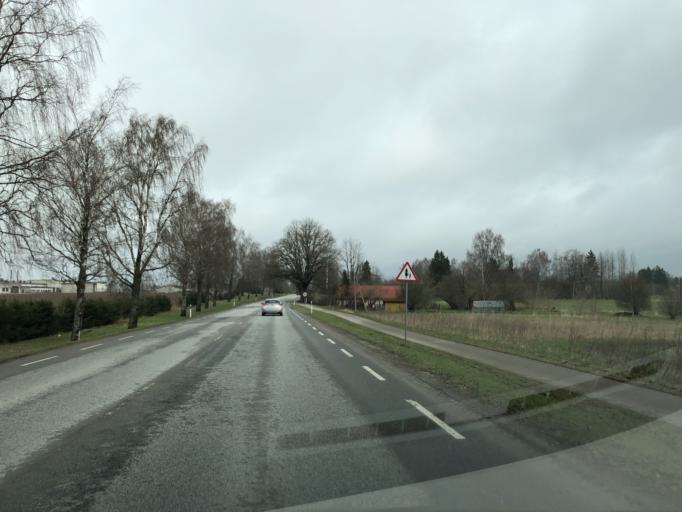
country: EE
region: Jogevamaa
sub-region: Jogeva linn
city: Jogeva
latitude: 58.7341
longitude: 26.3767
